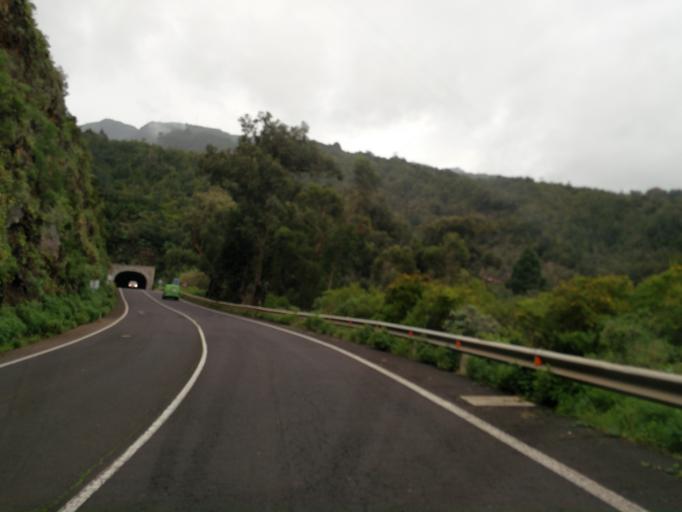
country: ES
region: Canary Islands
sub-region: Provincia de Santa Cruz de Tenerife
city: Garachico
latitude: 28.7573
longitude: -17.7612
